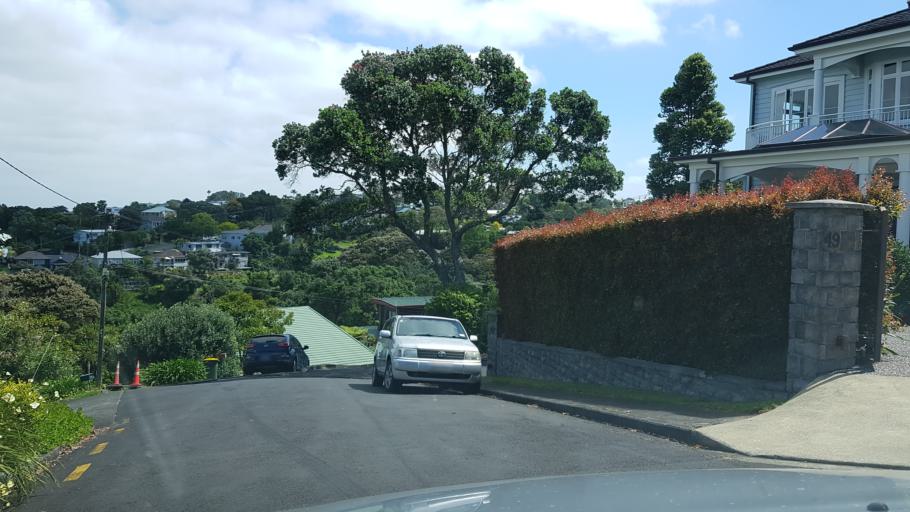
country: NZ
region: Auckland
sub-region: Auckland
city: North Shore
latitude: -36.8141
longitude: 174.7386
